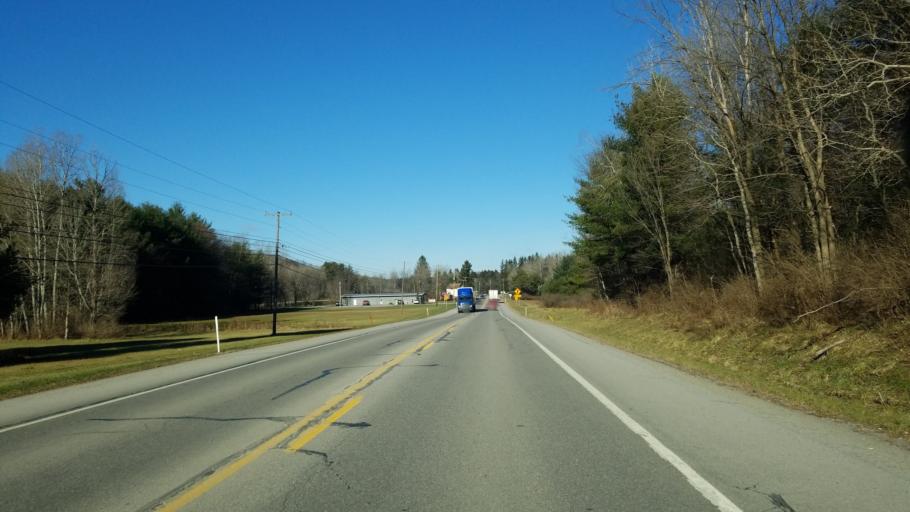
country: US
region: Pennsylvania
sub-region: Jefferson County
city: Brockway
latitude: 41.2156
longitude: -78.7740
